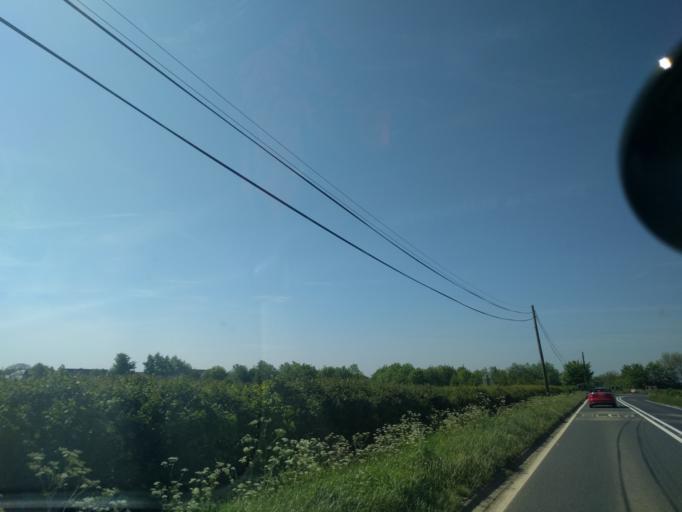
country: GB
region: England
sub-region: Somerset
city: Ilchester
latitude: 51.0598
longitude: -2.6363
